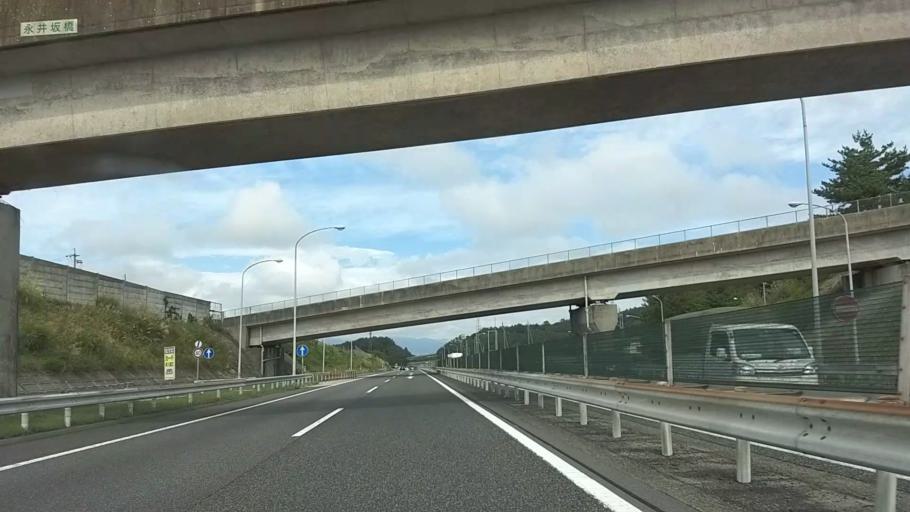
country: JP
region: Nagano
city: Shiojiri
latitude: 36.0973
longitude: 137.9973
